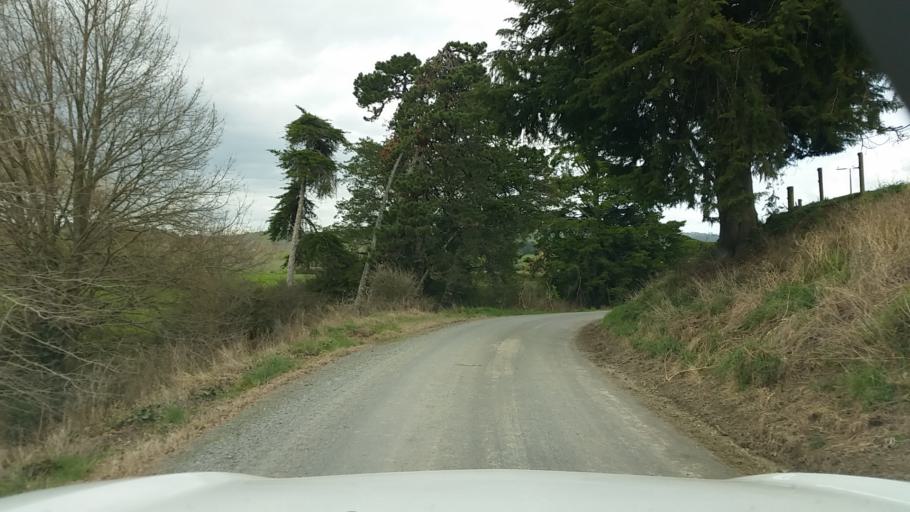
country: NZ
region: Waikato
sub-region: Hauraki District
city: Ngatea
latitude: -37.5055
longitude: 175.4409
